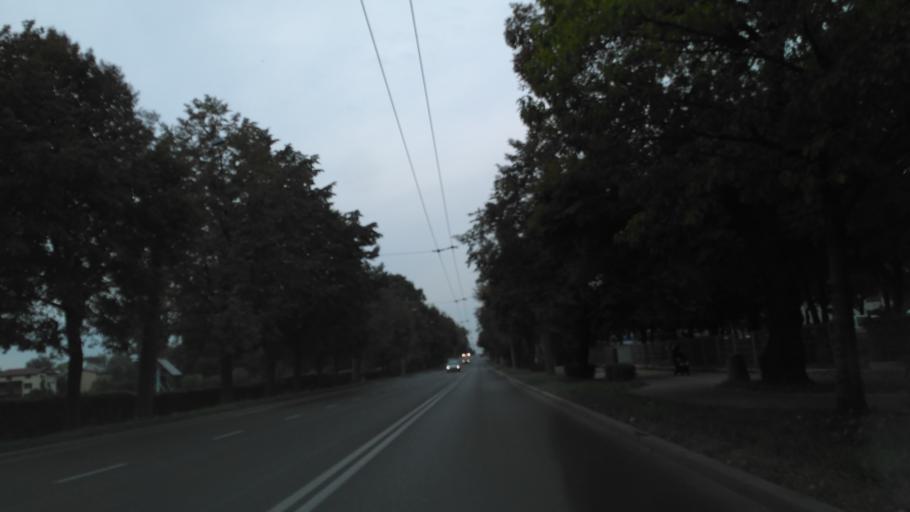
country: PL
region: Lublin Voivodeship
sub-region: Powiat lubelski
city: Lublin
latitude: 51.2277
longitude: 22.6014
